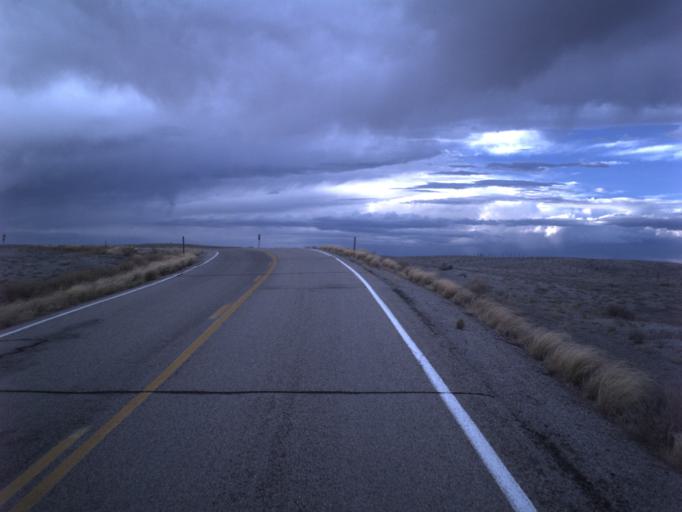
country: US
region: Utah
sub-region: Grand County
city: Moab
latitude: 38.8940
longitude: -109.3110
